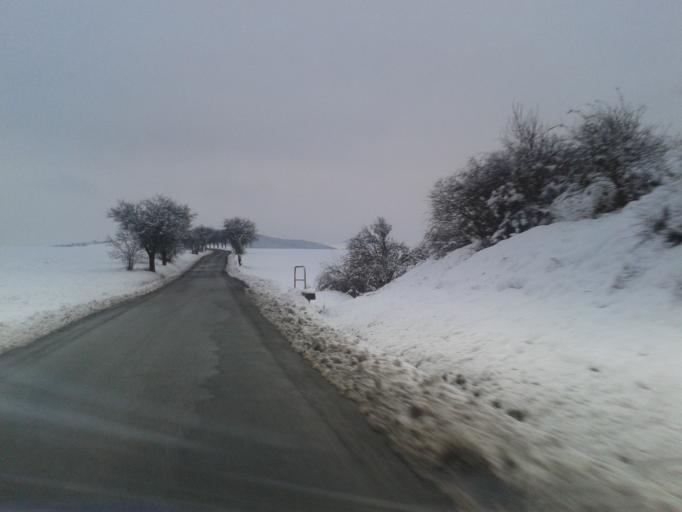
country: CZ
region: Central Bohemia
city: Revnice
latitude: 49.9180
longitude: 14.1598
